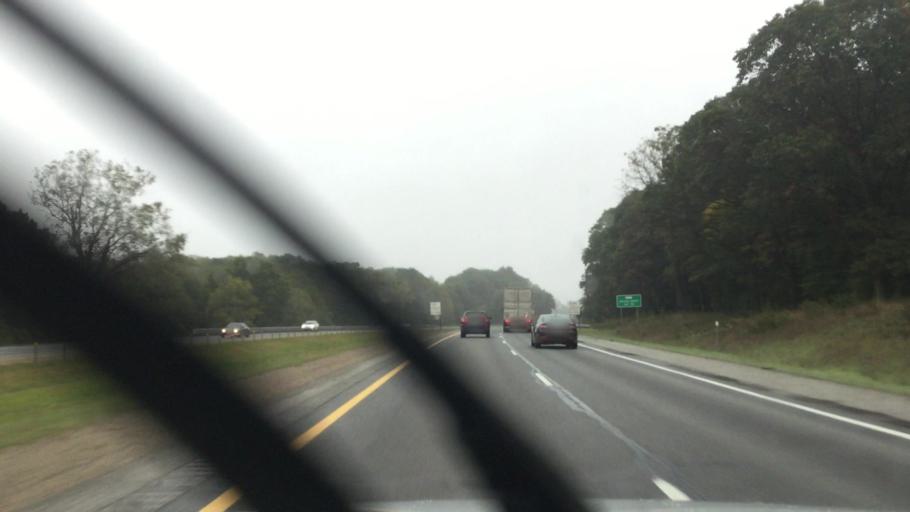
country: US
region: Michigan
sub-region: Van Buren County
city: Mattawan
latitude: 42.2372
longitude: -85.7009
